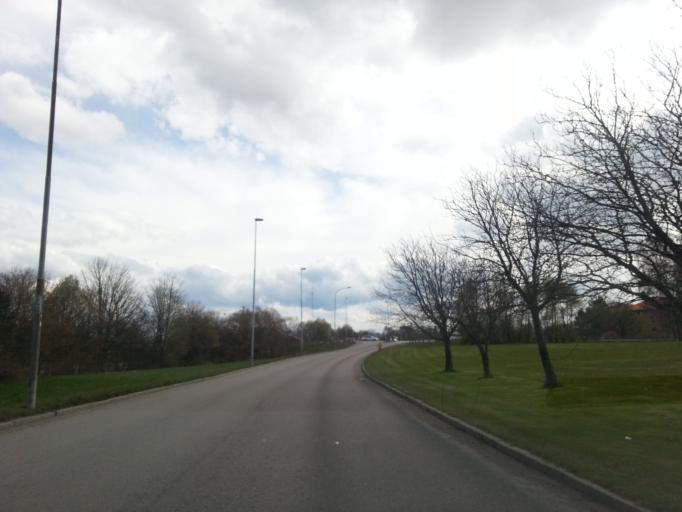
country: SE
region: Vaestra Goetaland
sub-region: Kungalvs Kommun
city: Kungalv
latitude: 57.8728
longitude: 11.9644
